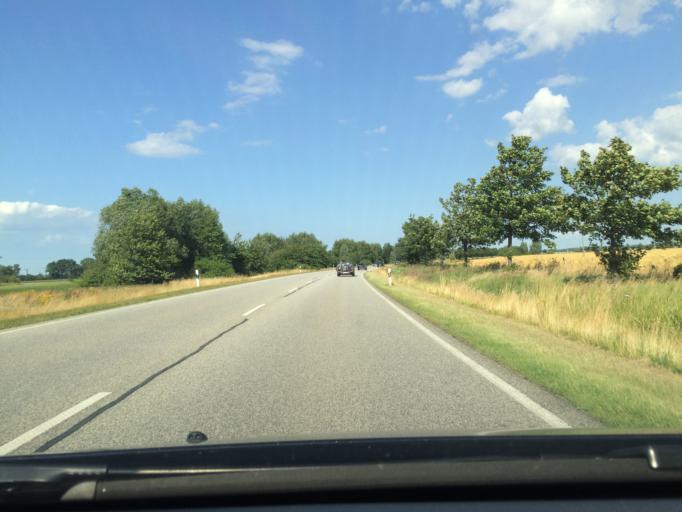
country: DE
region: Mecklenburg-Vorpommern
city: Bentwisch
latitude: 54.1267
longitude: 12.2068
